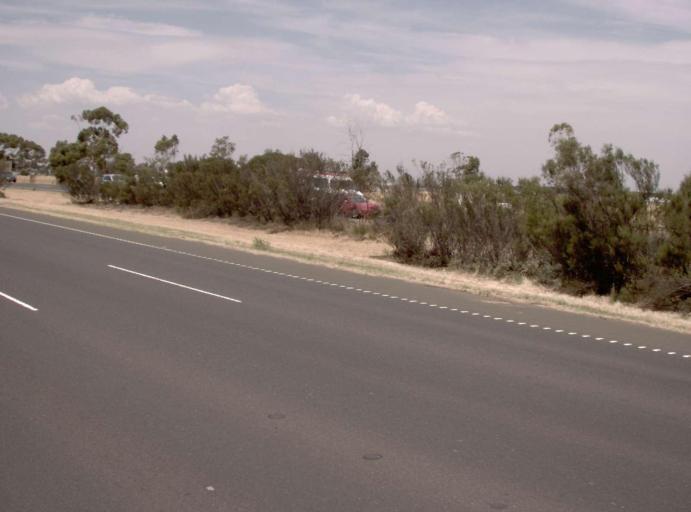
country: AU
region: Victoria
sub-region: Hobsons Bay
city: Laverton
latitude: -37.8389
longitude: 144.7967
